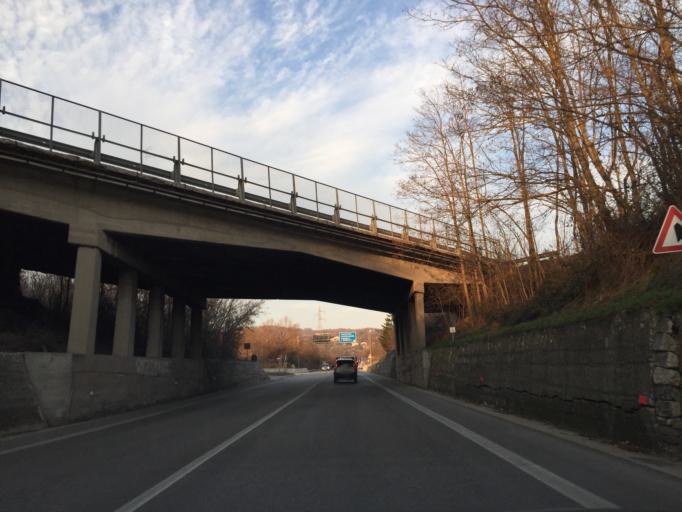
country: IT
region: Molise
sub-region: Provincia di Campobasso
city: Vinchiaturo
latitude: 41.4913
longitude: 14.6016
